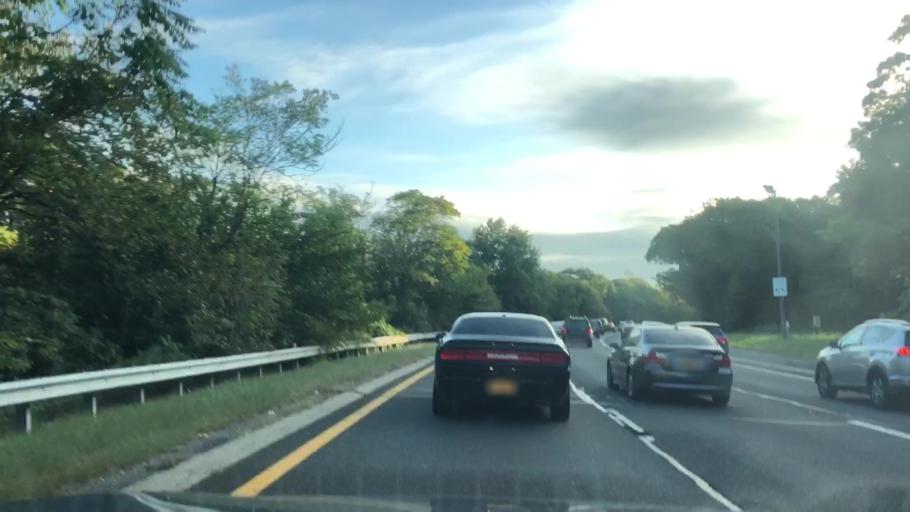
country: US
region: New York
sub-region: Nassau County
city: Uniondale
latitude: 40.6903
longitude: -73.5889
